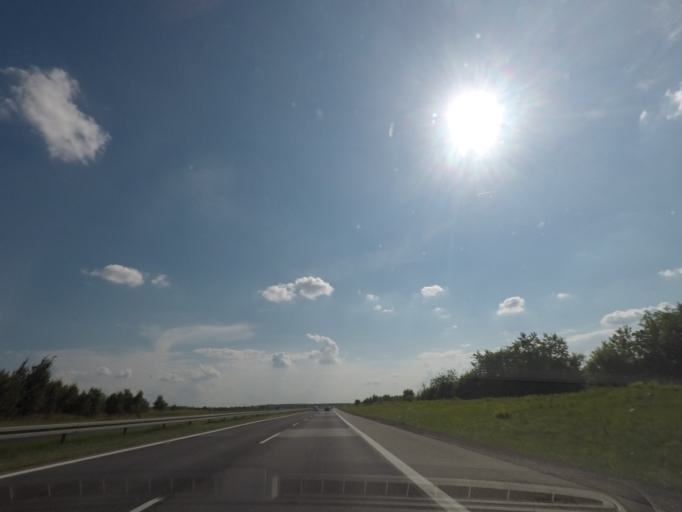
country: PL
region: Silesian Voivodeship
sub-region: Powiat czestochowski
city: Koscielec
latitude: 50.9129
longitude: 19.2131
